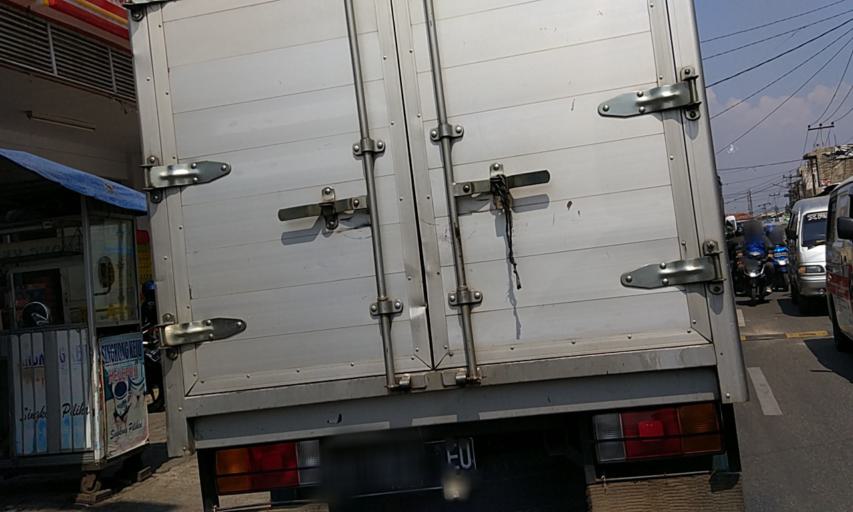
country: ID
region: West Java
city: Cimahi
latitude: -6.9108
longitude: 107.5613
